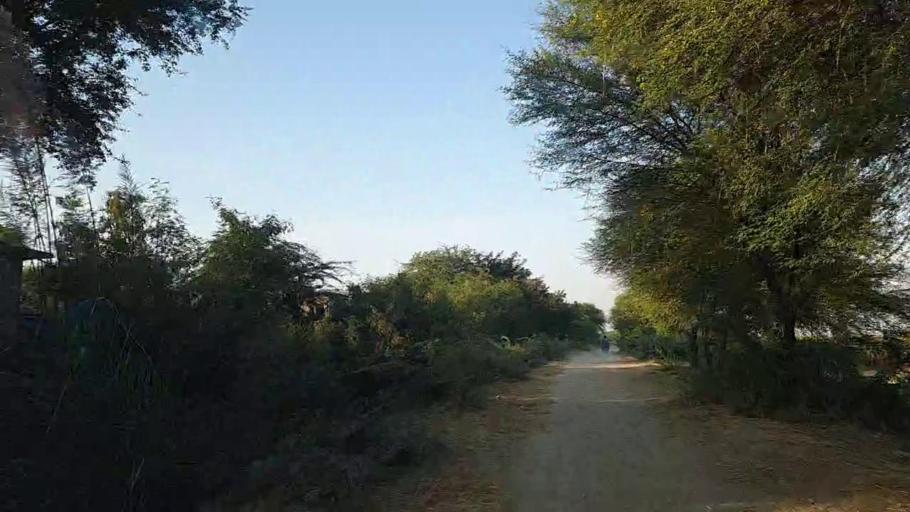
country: PK
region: Sindh
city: Mirpur Batoro
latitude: 24.7127
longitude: 68.2145
